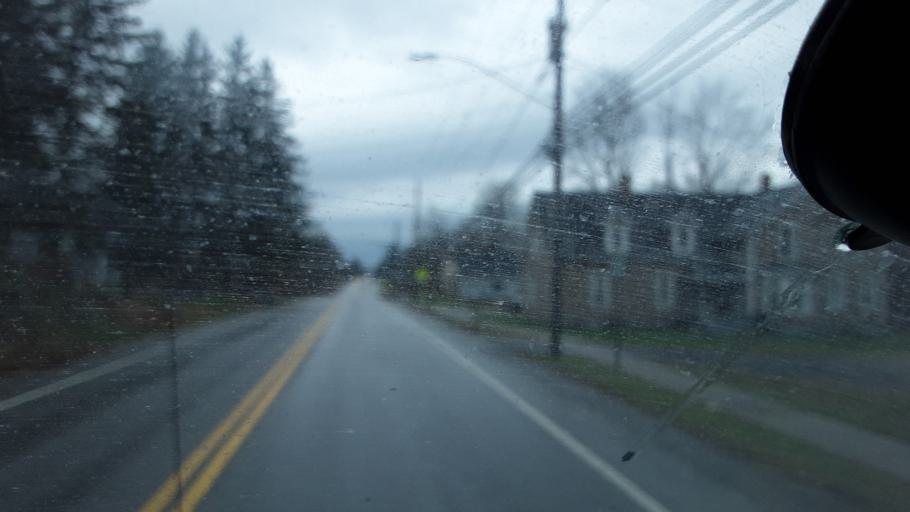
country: US
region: New York
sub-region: Erie County
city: Holland
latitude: 42.6486
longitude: -78.5495
